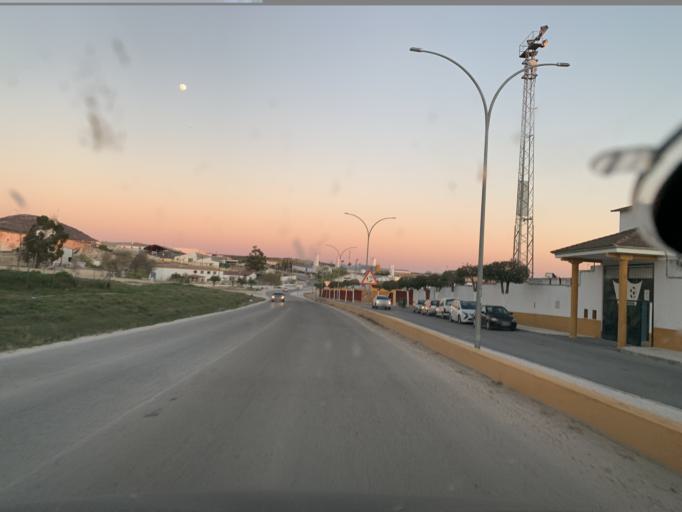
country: ES
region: Andalusia
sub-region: Provincia de Sevilla
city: Pedrera
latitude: 37.2305
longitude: -4.8956
